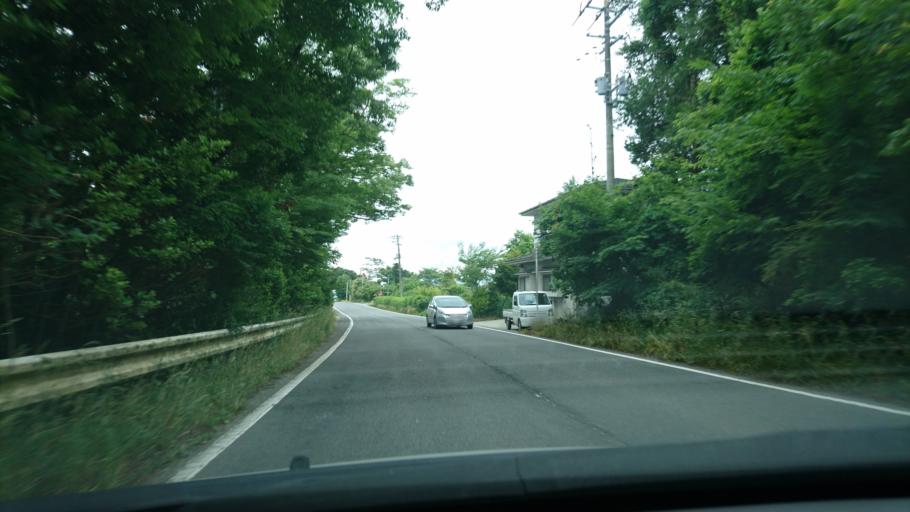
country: JP
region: Iwate
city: Ichinoseki
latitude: 38.7554
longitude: 141.2553
